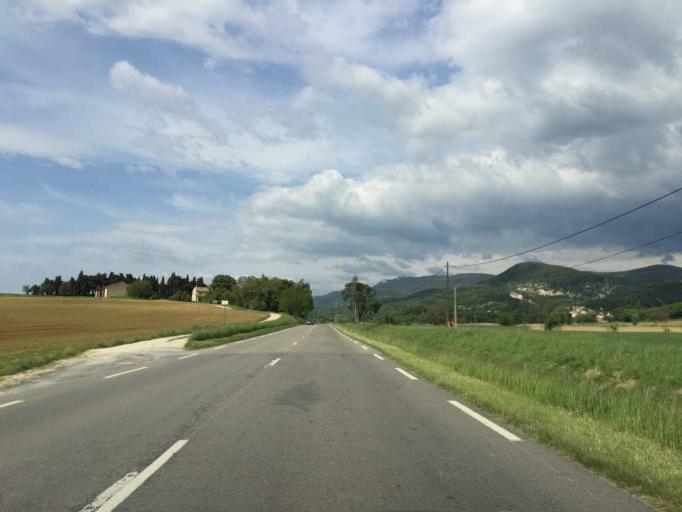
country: FR
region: Rhone-Alpes
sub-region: Departement de la Drome
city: Eurre
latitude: 44.7603
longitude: 5.0193
